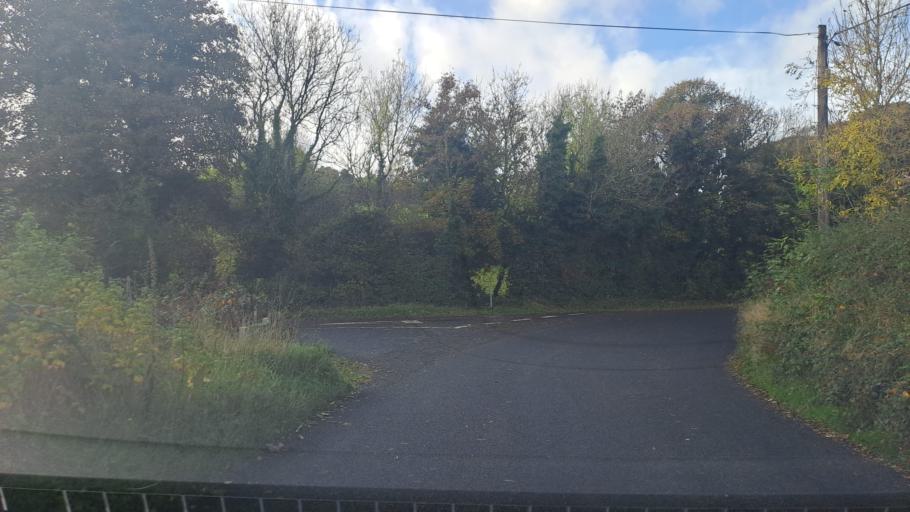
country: IE
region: Ulster
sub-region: An Cabhan
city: Cootehill
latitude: 54.0333
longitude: -7.0068
